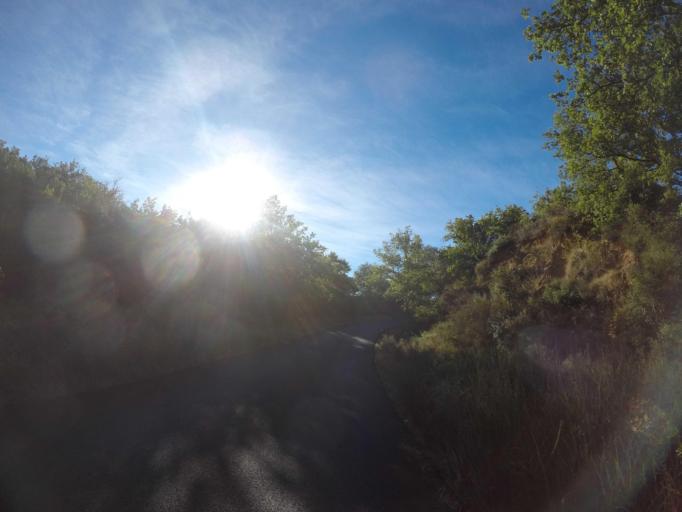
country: FR
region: Languedoc-Roussillon
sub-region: Departement des Pyrenees-Orientales
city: Llupia
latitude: 42.5989
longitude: 2.7651
